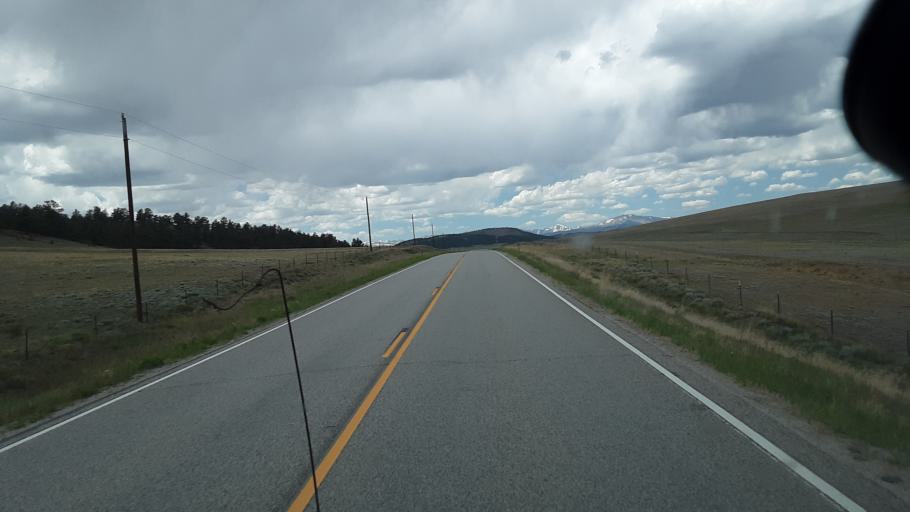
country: US
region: Colorado
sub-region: Park County
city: Fairplay
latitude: 39.0061
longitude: -105.7784
